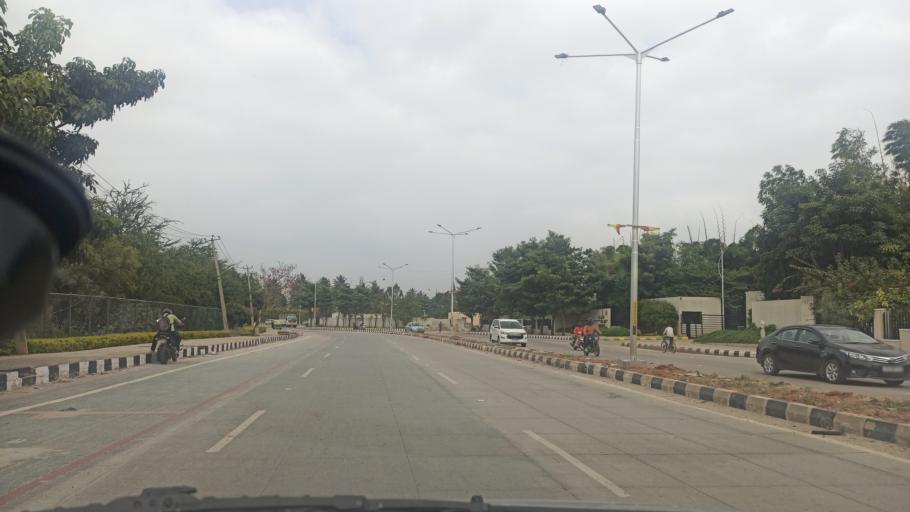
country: IN
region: Karnataka
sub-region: Bangalore Urban
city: Yelahanka
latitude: 13.0451
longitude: 77.6123
